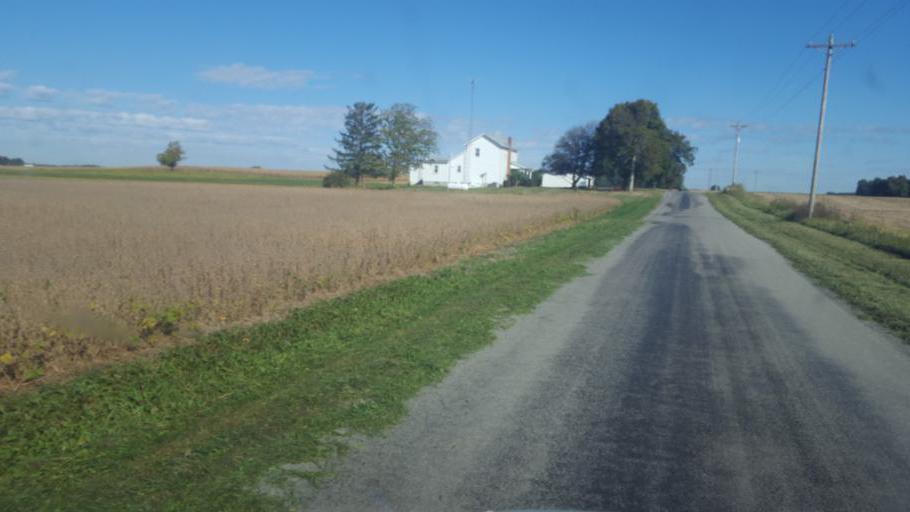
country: US
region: Ohio
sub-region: Wyandot County
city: Upper Sandusky
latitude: 40.7870
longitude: -83.2173
